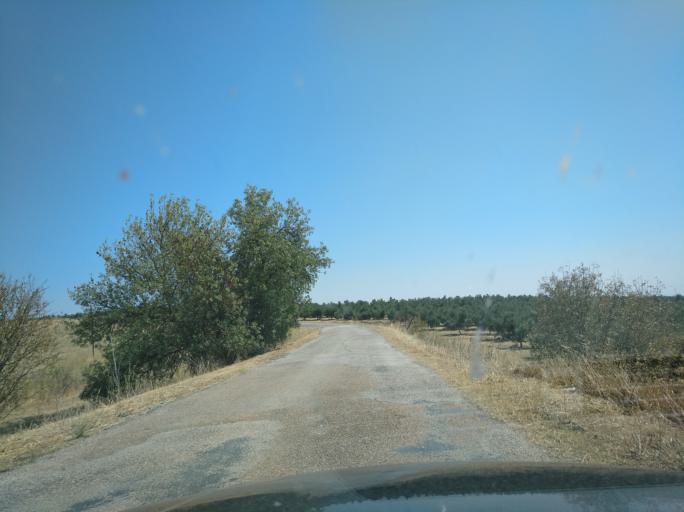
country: PT
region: Portalegre
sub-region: Campo Maior
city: Campo Maior
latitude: 38.9836
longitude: -7.0986
